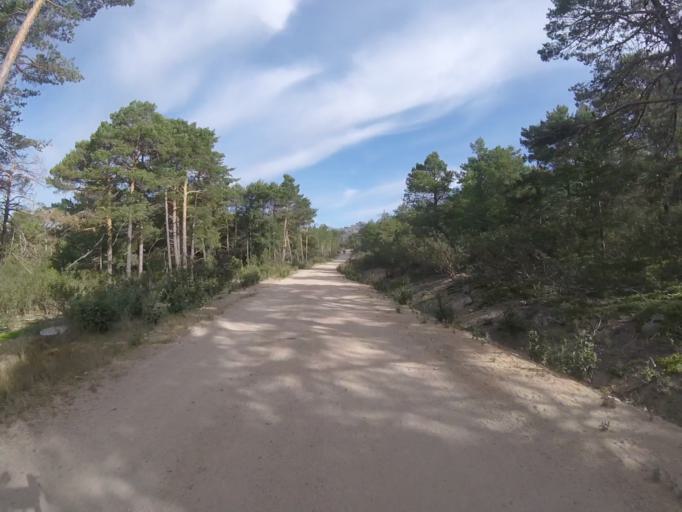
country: ES
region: Castille and Leon
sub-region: Provincia de Avila
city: Peguerinos
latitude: 40.6552
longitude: -4.1846
